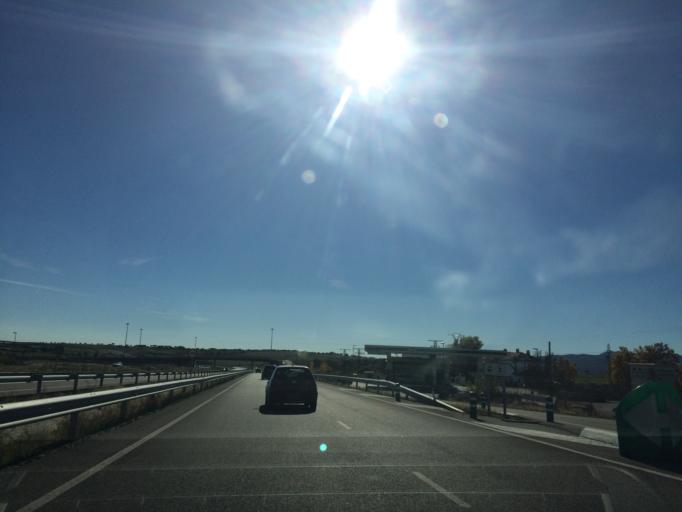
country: ES
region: Madrid
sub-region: Provincia de Madrid
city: Colmenar Viejo
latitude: 40.7189
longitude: -3.7922
